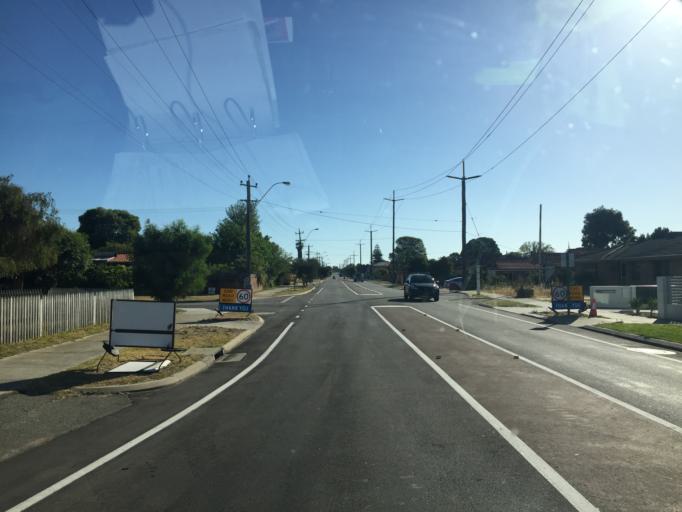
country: AU
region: Western Australia
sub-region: Belmont
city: Rivervale
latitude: -31.9616
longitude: 115.9277
